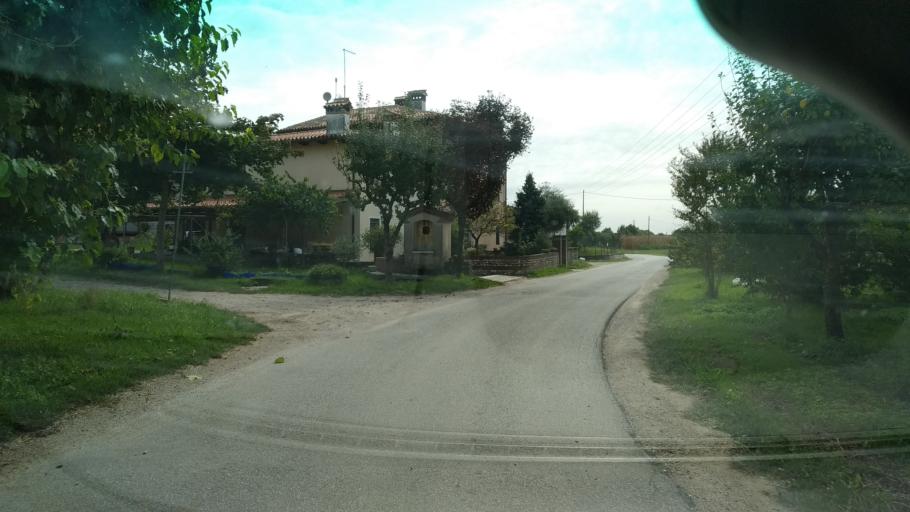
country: IT
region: Veneto
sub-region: Provincia di Vicenza
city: Sandrigo
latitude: 45.6412
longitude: 11.5925
